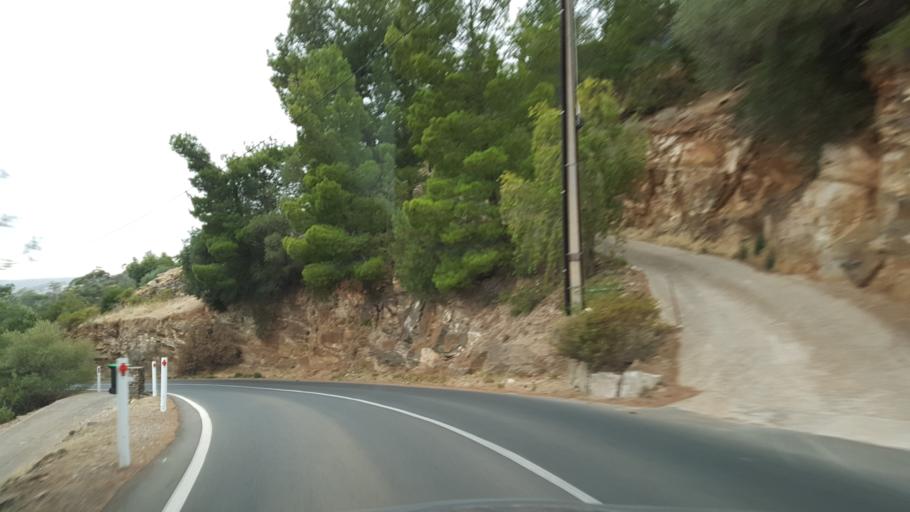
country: AU
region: South Australia
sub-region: Burnside
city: Mount Osmond
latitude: -34.9615
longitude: 138.6516
